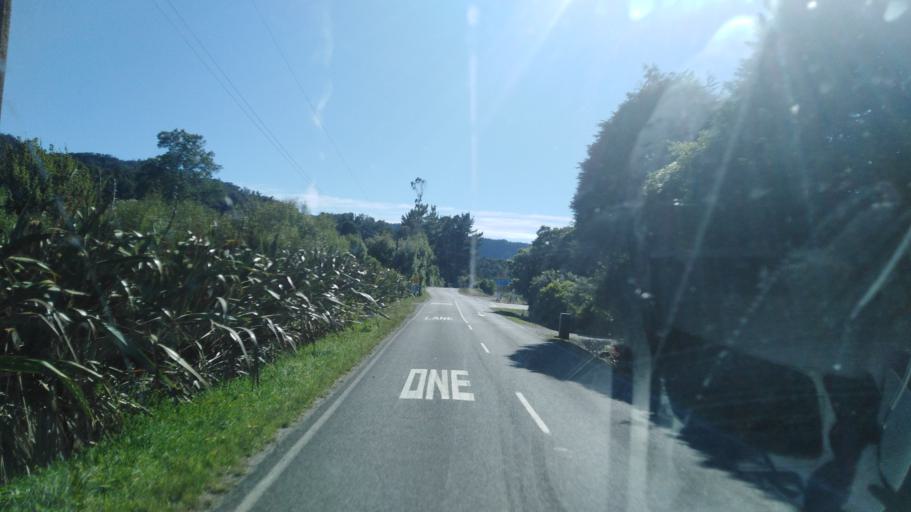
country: NZ
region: West Coast
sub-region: Buller District
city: Westport
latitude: -41.5306
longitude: 171.9650
